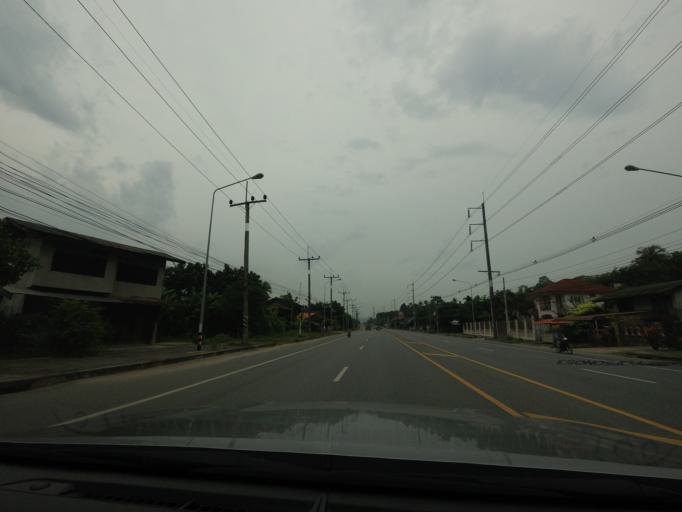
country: TH
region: Songkhla
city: Na Mom
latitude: 7.0615
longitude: 100.6439
